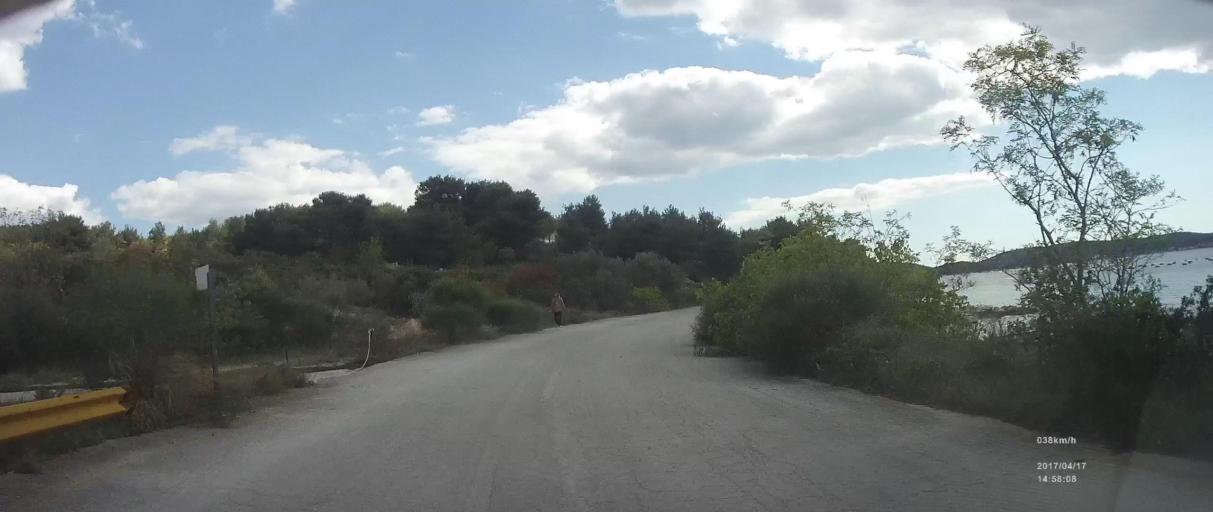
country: HR
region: Sibensko-Kniniska
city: Murter
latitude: 43.8404
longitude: 15.6280
